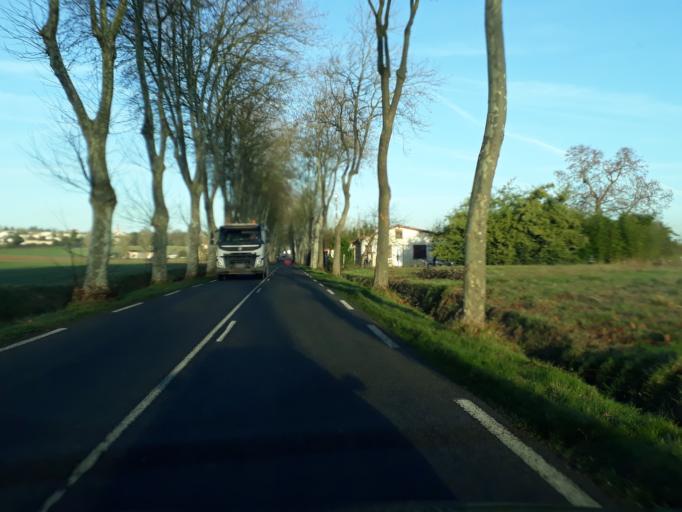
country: FR
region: Midi-Pyrenees
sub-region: Departement de la Haute-Garonne
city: Rieumes
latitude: 43.4093
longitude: 1.1346
